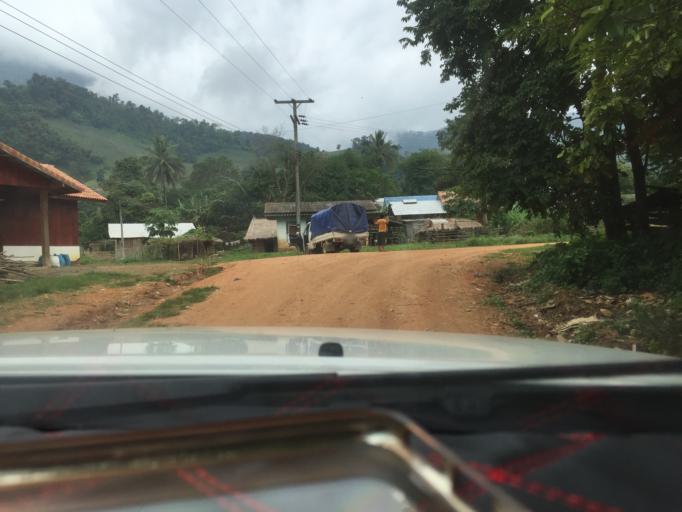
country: TH
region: Phayao
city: Phu Sang
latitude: 19.7439
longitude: 100.4311
